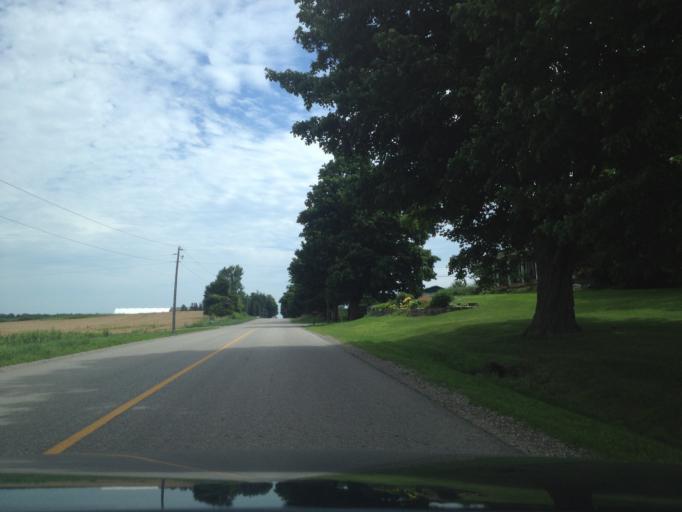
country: CA
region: Ontario
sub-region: Oxford County
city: Woodstock
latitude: 42.9908
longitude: -80.6738
